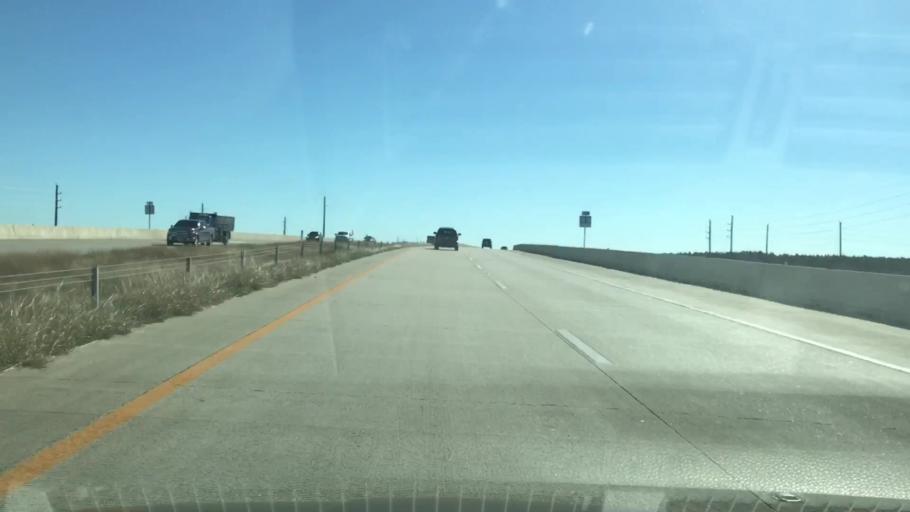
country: US
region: Texas
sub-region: Harris County
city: Cypress
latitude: 29.9063
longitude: -95.7592
